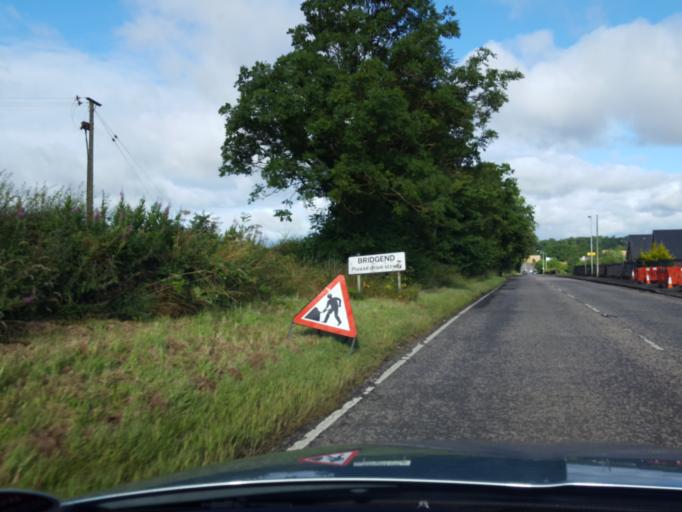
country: GB
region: Scotland
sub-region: West Lothian
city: Livingston
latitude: 55.9664
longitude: -3.5274
